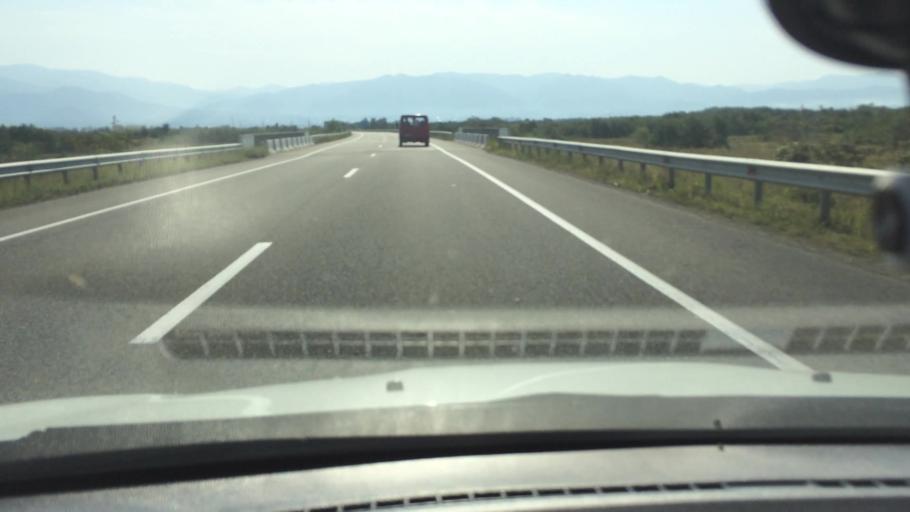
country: GE
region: Guria
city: Urek'i
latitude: 41.9142
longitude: 41.7786
